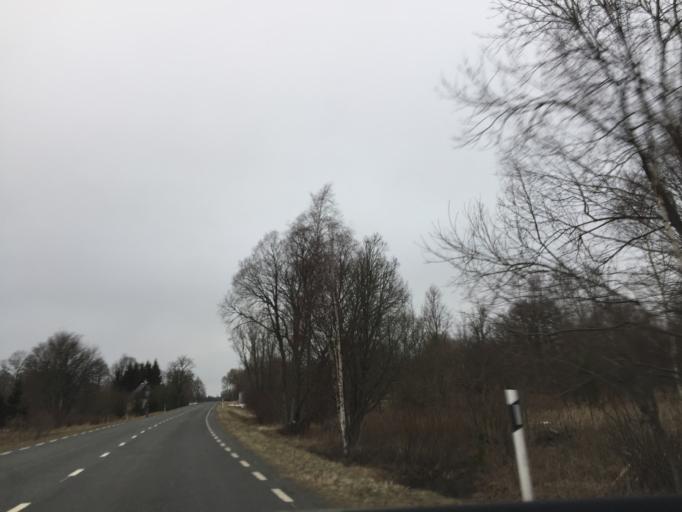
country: EE
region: Saare
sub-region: Kuressaare linn
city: Kuressaare
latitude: 58.5296
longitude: 22.3425
